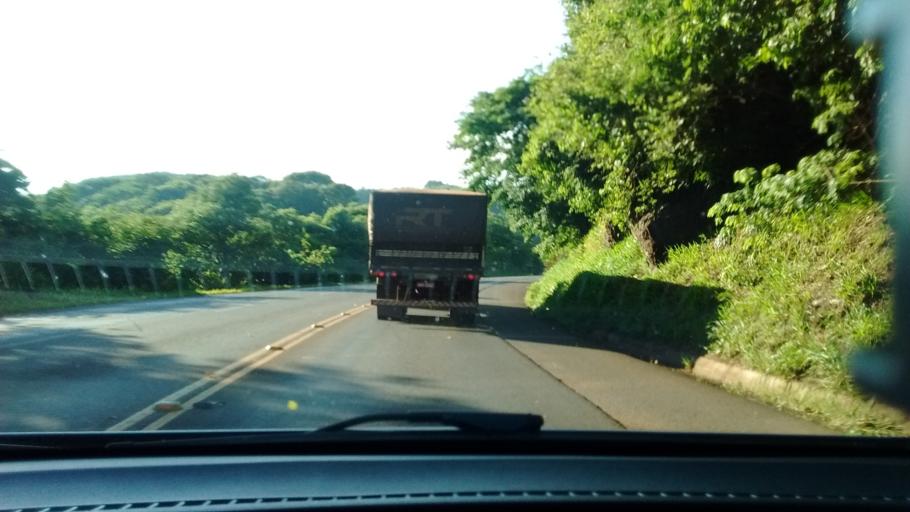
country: BR
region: Parana
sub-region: Cascavel
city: Cascavel
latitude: -25.2030
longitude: -53.5980
